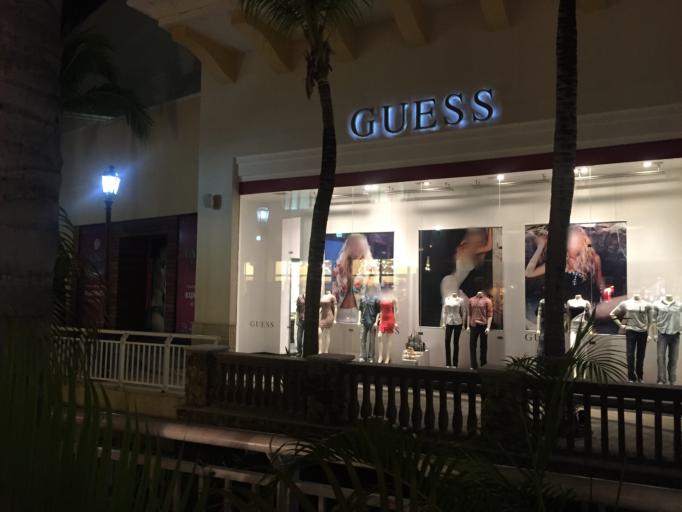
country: MX
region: Guerrero
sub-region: Acapulco de Juarez
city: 10 de Abril
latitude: 16.7729
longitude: -99.7758
